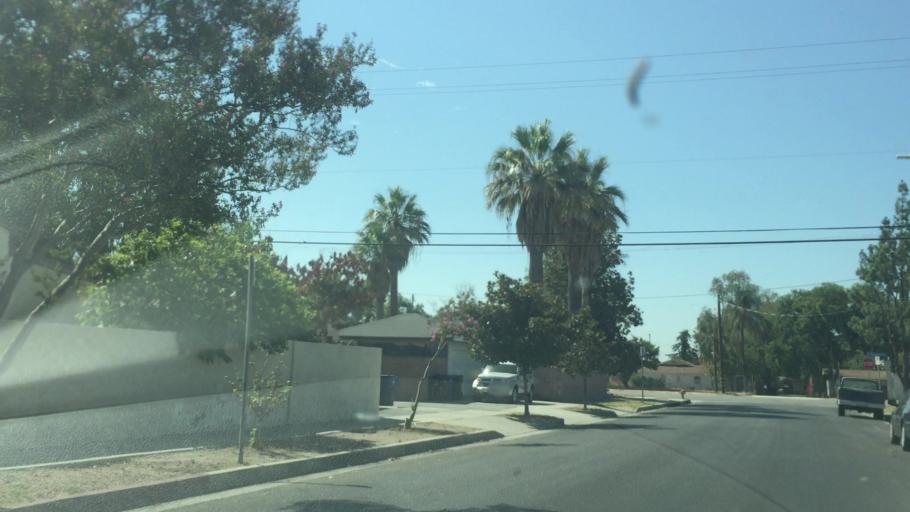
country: US
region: California
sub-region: Los Angeles County
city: San Fernando
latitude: 34.2581
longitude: -118.4783
